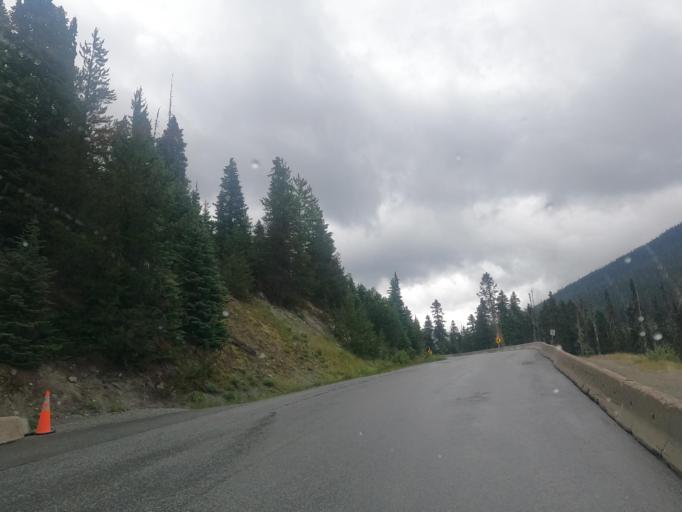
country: CA
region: British Columbia
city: Pemberton
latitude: 50.3849
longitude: -122.4687
